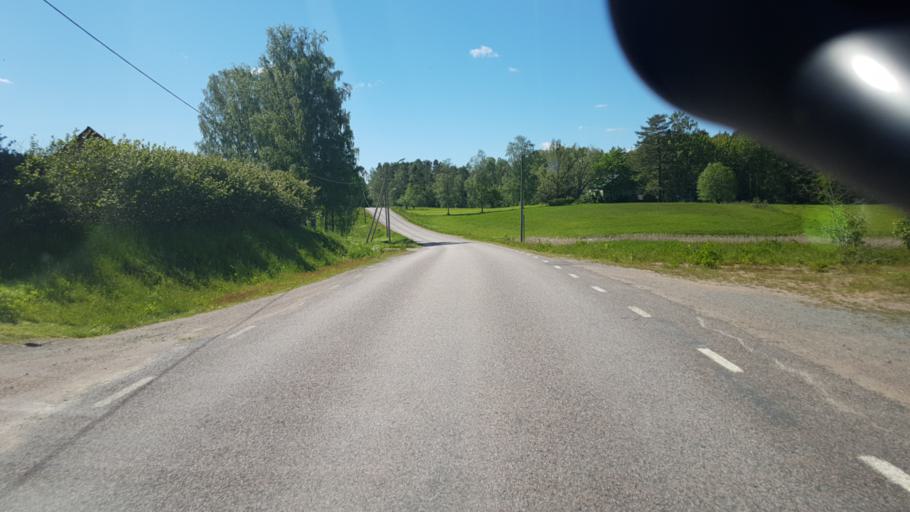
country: SE
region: Vaermland
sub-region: Grums Kommun
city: Slottsbron
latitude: 59.4737
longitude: 12.8816
